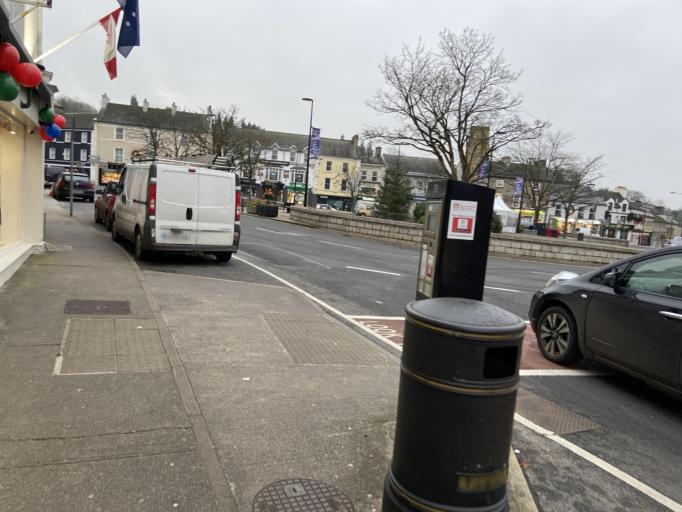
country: IE
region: Ulster
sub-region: County Donegal
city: Donegal
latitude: 54.6543
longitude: -8.1105
